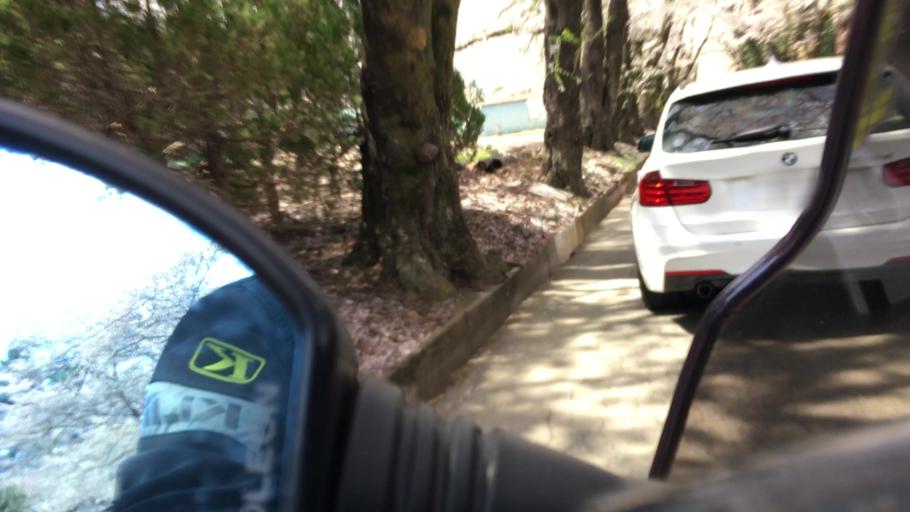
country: JP
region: Yamanashi
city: Nirasaki
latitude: 35.7768
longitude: 138.3445
